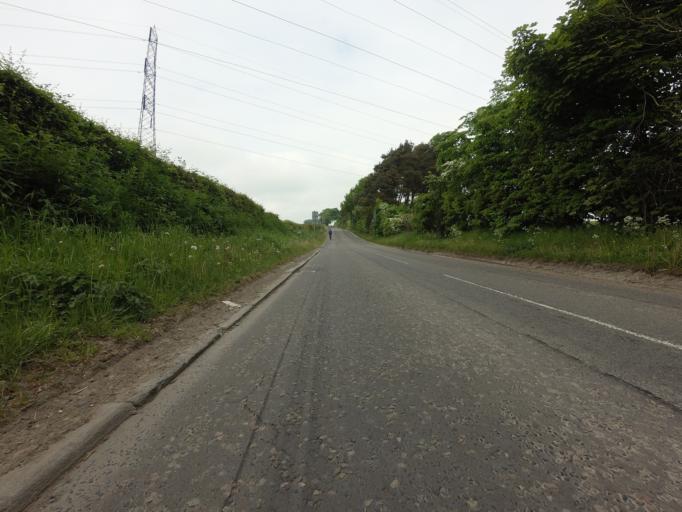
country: GB
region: Scotland
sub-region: Fife
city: Townhill
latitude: 56.0943
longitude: -3.4421
